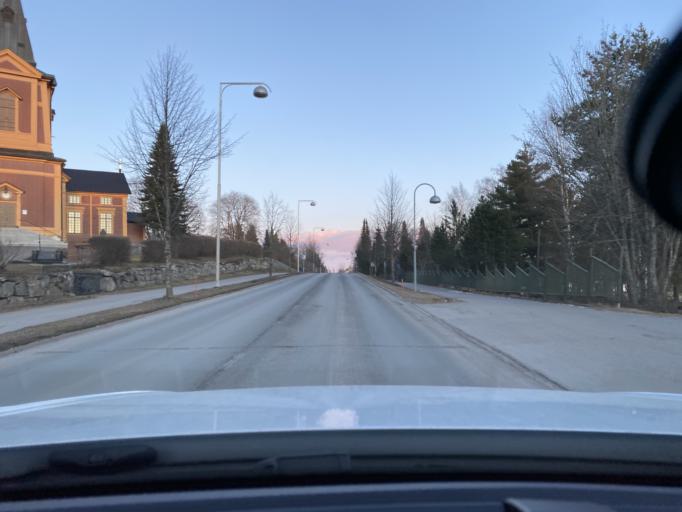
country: FI
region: Pirkanmaa
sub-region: Lounais-Pirkanmaa
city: Punkalaidun
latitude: 61.1148
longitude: 23.0948
